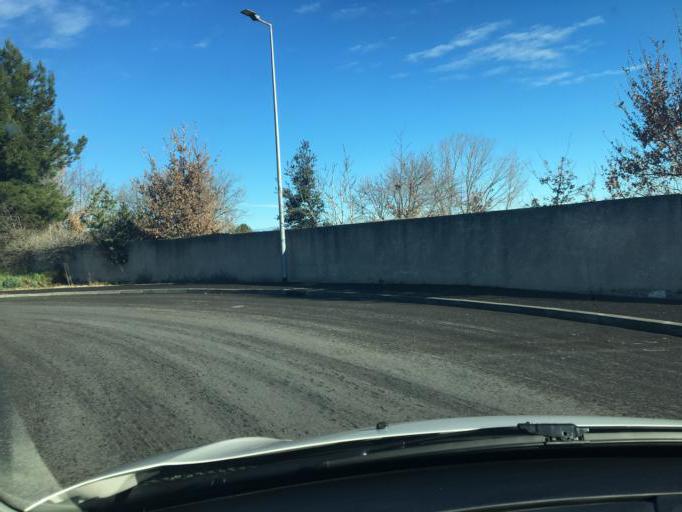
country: FR
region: Provence-Alpes-Cote d'Azur
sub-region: Departement des Bouches-du-Rhone
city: Cabries
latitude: 43.4853
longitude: 5.3623
